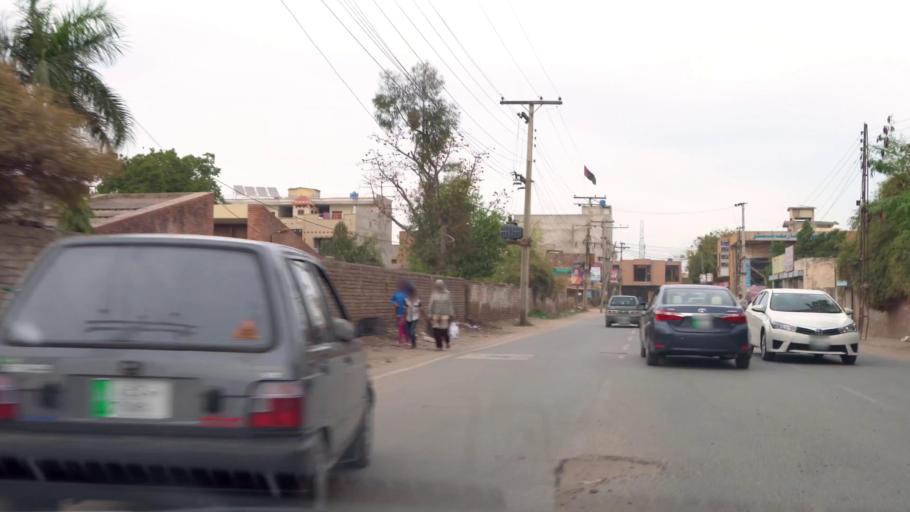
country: PK
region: Punjab
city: Sargodha
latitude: 32.0780
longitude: 72.6790
